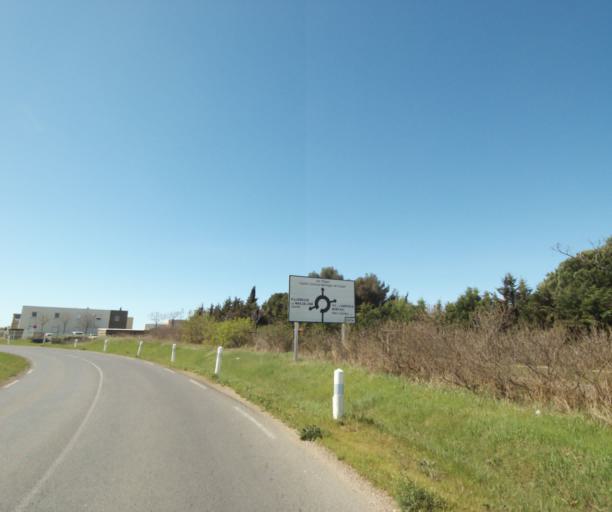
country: FR
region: Languedoc-Roussillon
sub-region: Departement de l'Herault
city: Villeneuve-les-Maguelone
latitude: 43.5341
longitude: 3.8520
